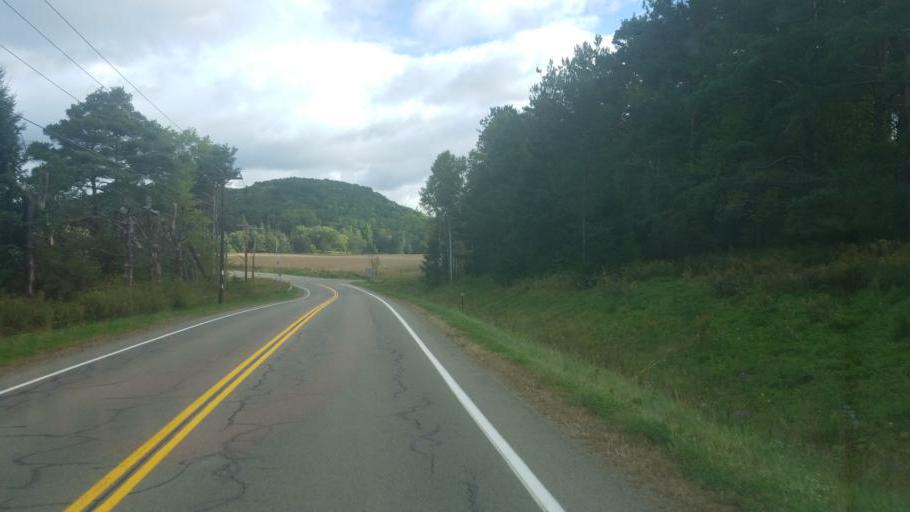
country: US
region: New York
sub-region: Cattaraugus County
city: Weston Mills
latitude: 42.0983
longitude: -78.3482
